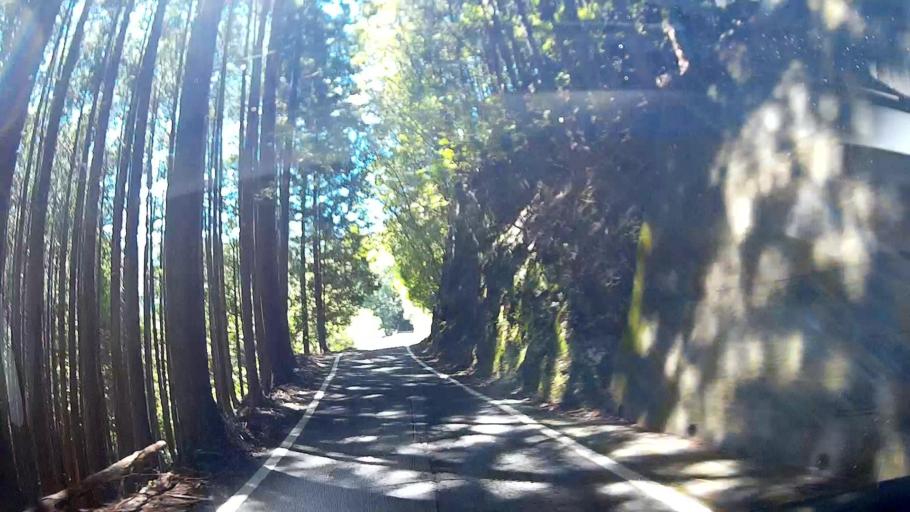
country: JP
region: Shizuoka
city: Shizuoka-shi
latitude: 35.1867
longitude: 138.2706
